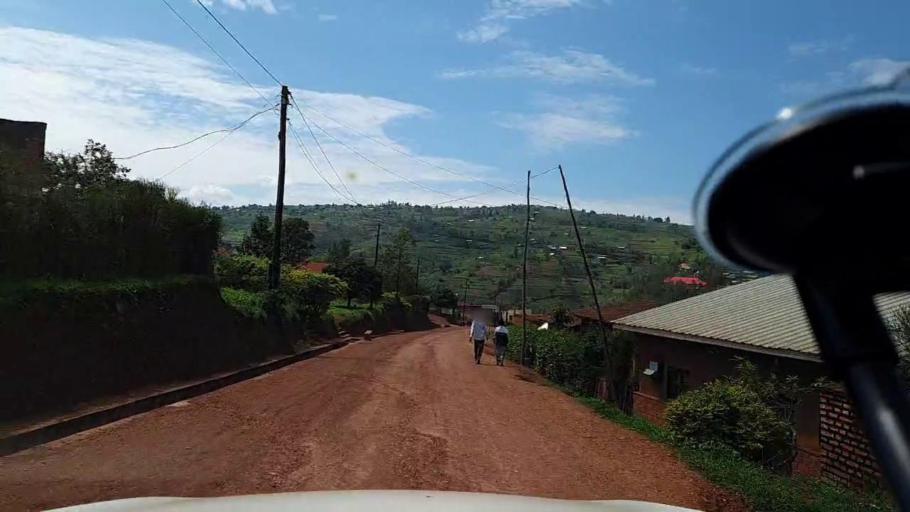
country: RW
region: Kigali
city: Kigali
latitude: -1.8010
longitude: 29.8947
